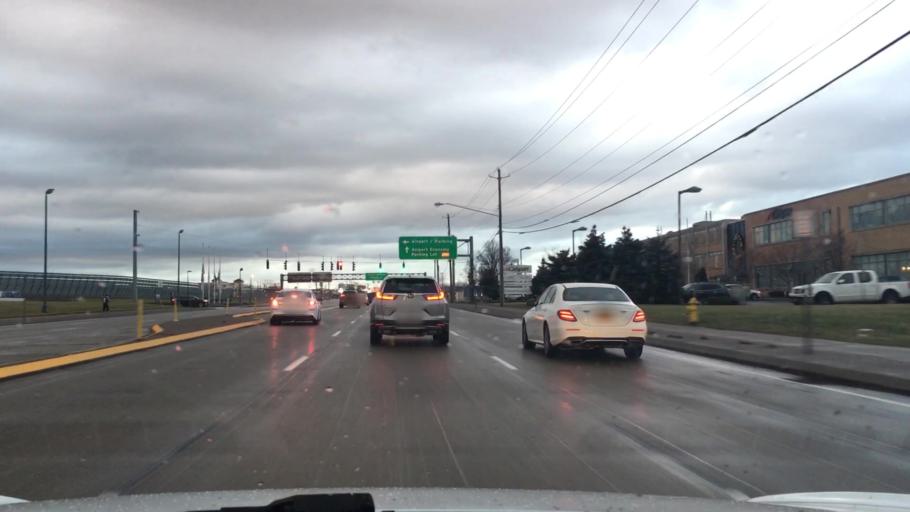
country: US
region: New York
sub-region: Erie County
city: Williamsville
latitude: 42.9332
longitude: -78.7234
